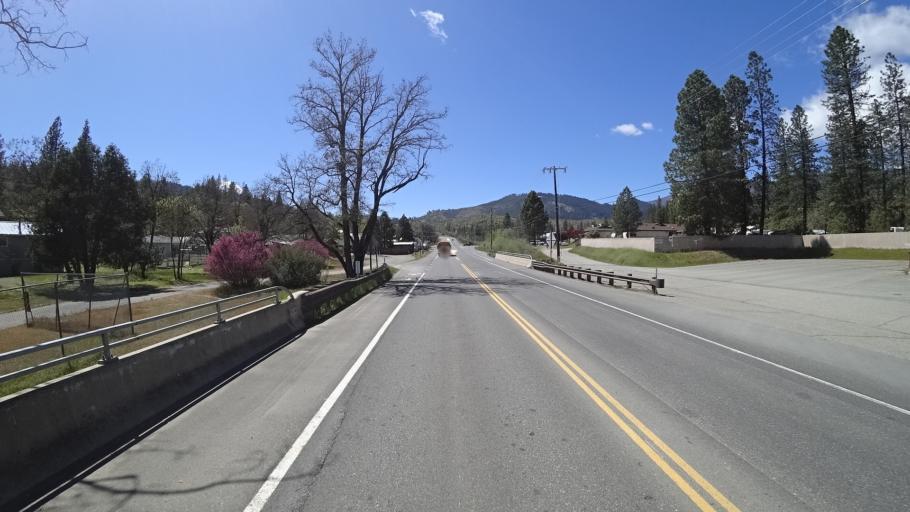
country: US
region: California
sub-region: Trinity County
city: Weaverville
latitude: 40.7356
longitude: -122.9450
